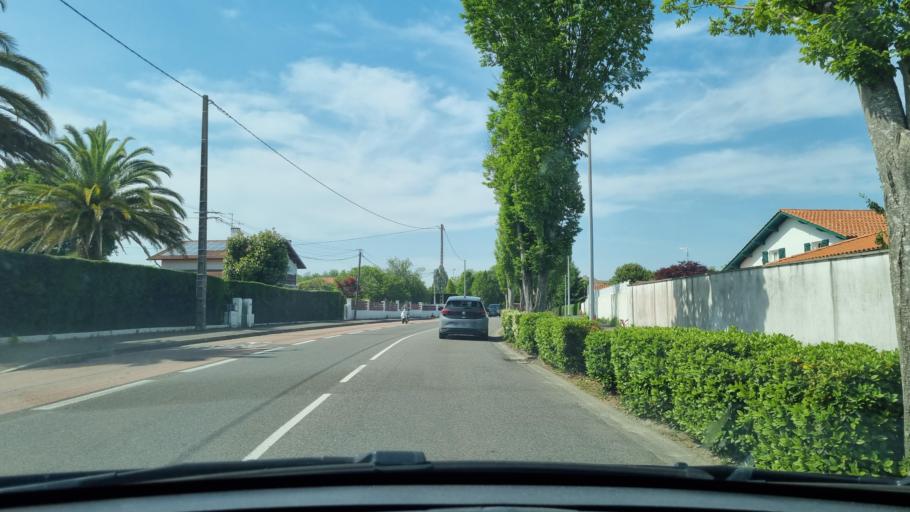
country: FR
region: Aquitaine
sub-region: Departement des Pyrenees-Atlantiques
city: Anglet
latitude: 43.4713
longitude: -1.4987
